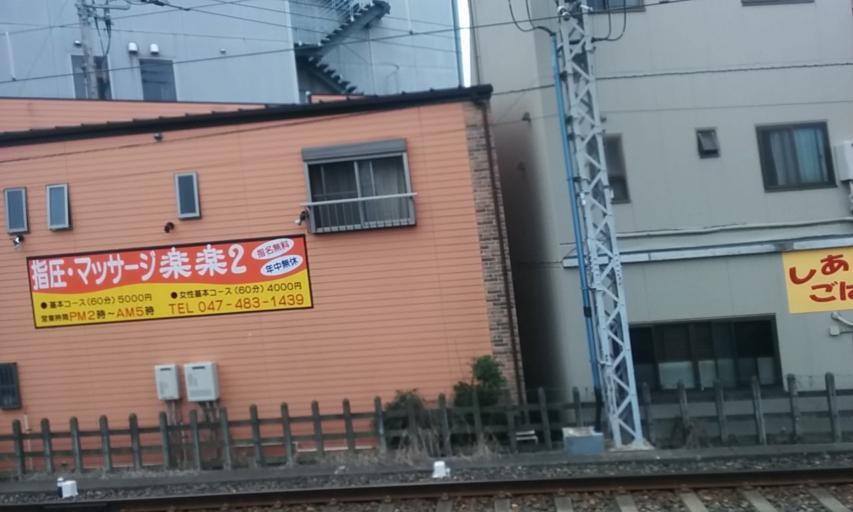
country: JP
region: Chiba
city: Yotsukaido
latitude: 35.7006
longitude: 140.0899
